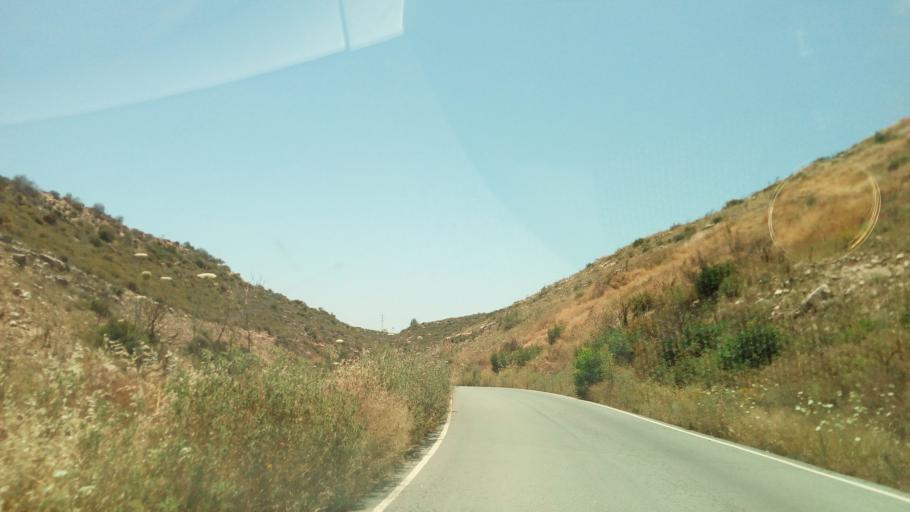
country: CY
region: Limassol
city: Ypsonas
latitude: 34.7279
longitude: 32.9503
